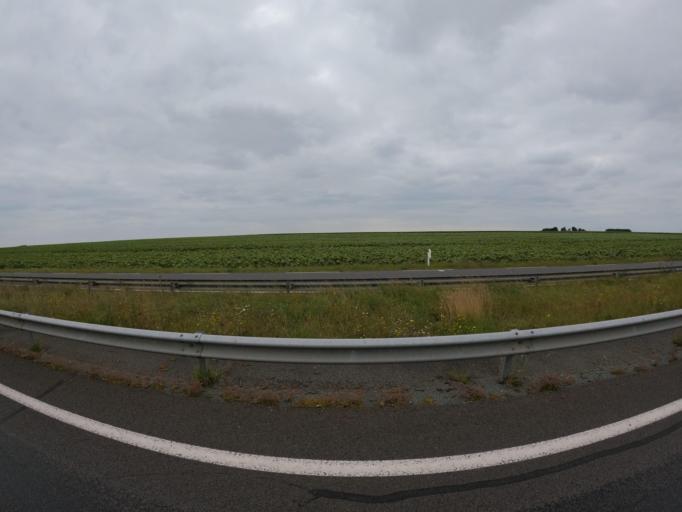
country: FR
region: Pays de la Loire
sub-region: Departement de la Vendee
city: Maillezais
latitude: 46.4195
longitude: -0.7059
